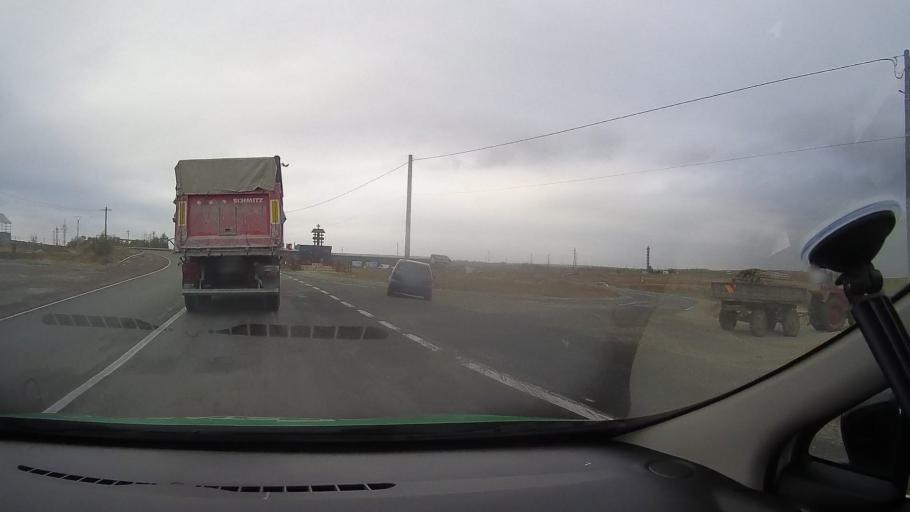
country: RO
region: Constanta
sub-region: Comuna Poarta Alba
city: Poarta Alba
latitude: 44.2130
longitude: 28.3942
